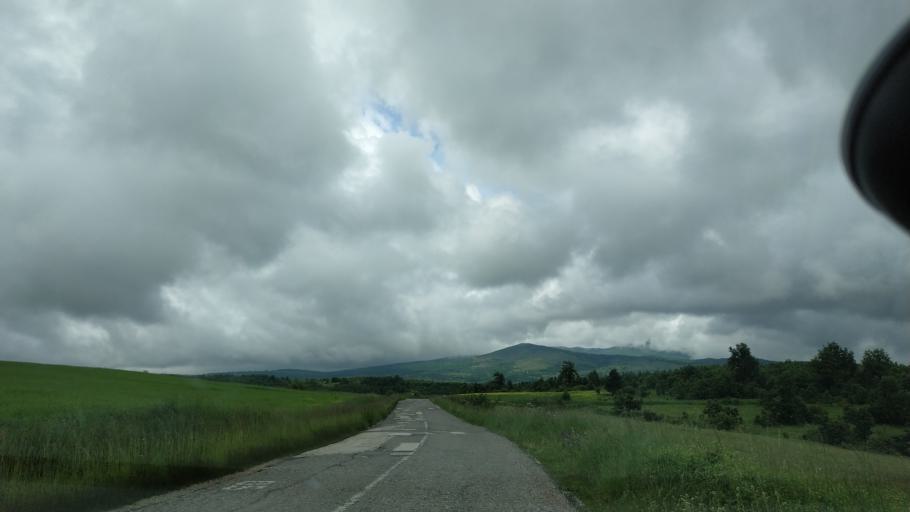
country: RS
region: Central Serbia
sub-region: Zajecarski Okrug
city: Soko Banja
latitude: 43.7007
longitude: 21.9368
